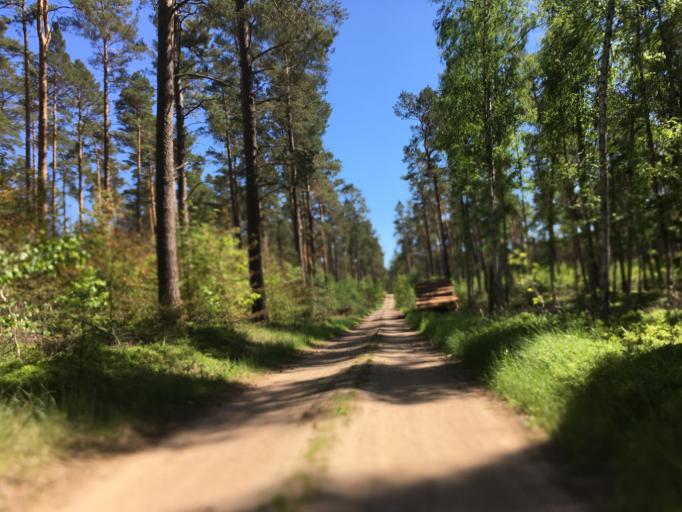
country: DE
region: Brandenburg
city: Friedrichswalde
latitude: 52.9907
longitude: 13.6078
